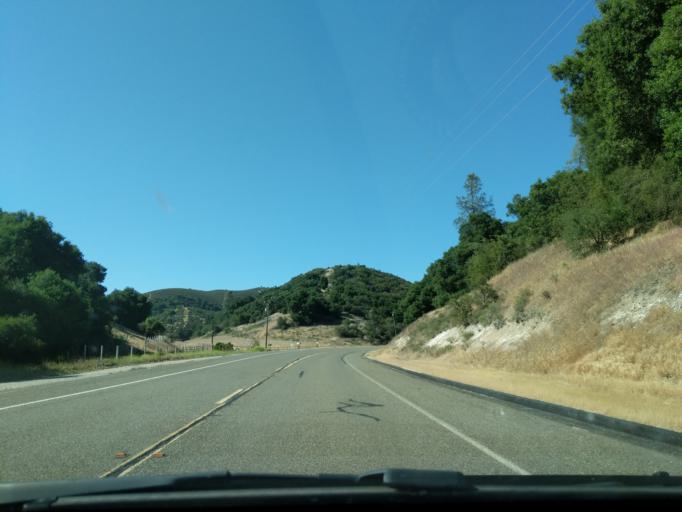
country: US
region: California
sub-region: Monterey County
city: King City
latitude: 36.0678
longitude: -121.1842
